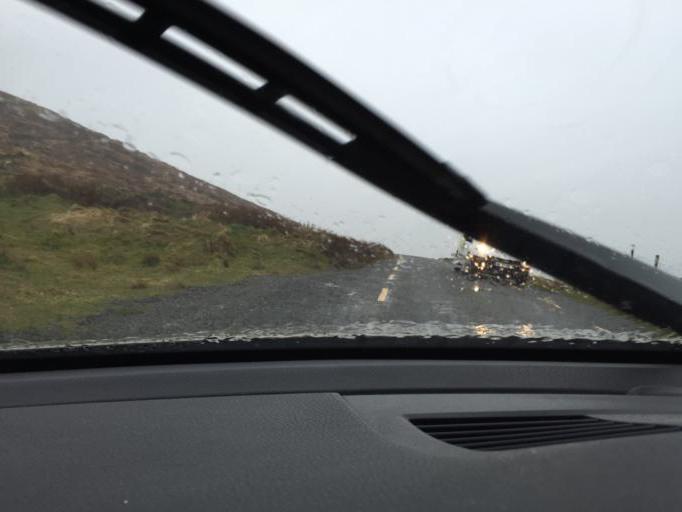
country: IE
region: Munster
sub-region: Ciarrai
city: Dingle
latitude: 52.1394
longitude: -10.4157
